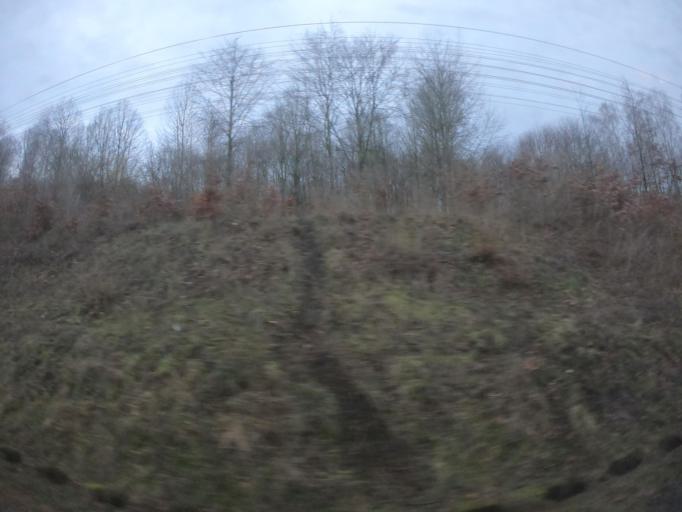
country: PL
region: West Pomeranian Voivodeship
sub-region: Powiat szczecinecki
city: Borne Sulinowo
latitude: 53.6411
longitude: 16.5067
